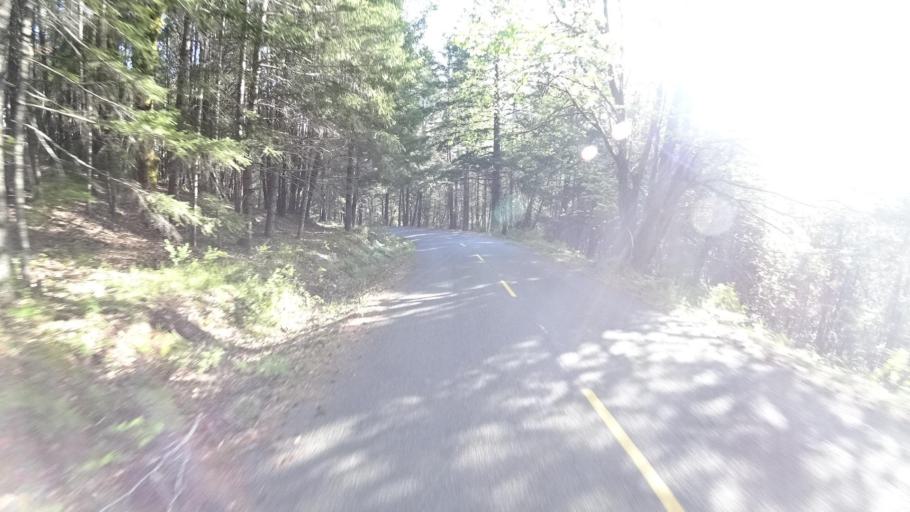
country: US
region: California
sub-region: Humboldt County
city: Rio Dell
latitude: 40.3302
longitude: -124.0342
